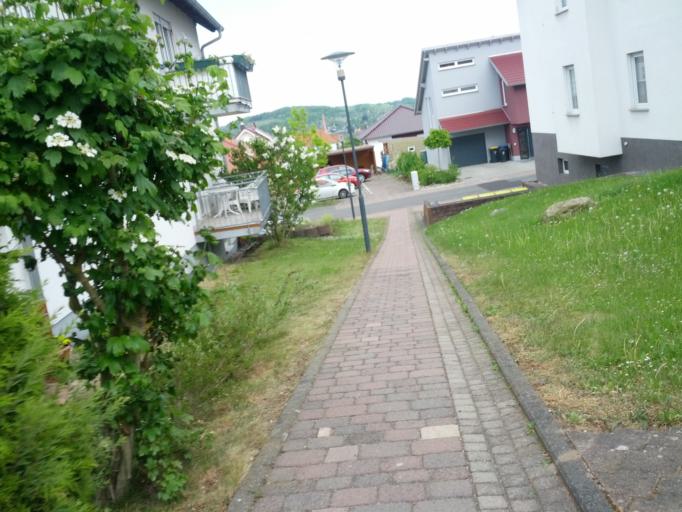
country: DE
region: Thuringia
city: Eisenach
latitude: 50.9931
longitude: 10.2899
